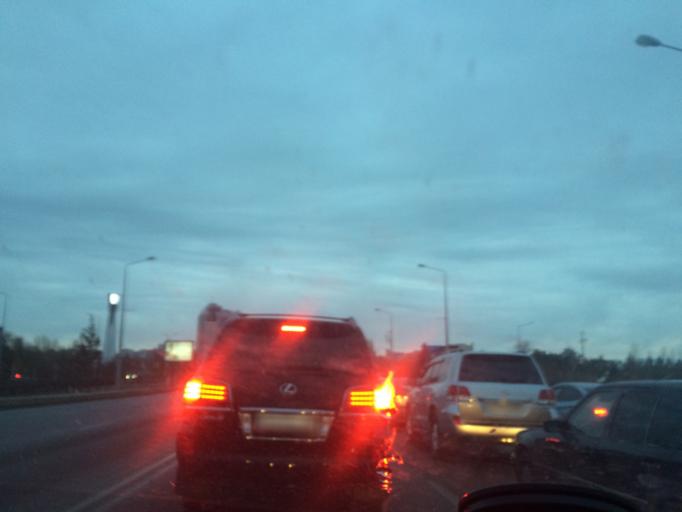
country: KZ
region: Astana Qalasy
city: Astana
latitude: 51.1557
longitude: 71.4119
